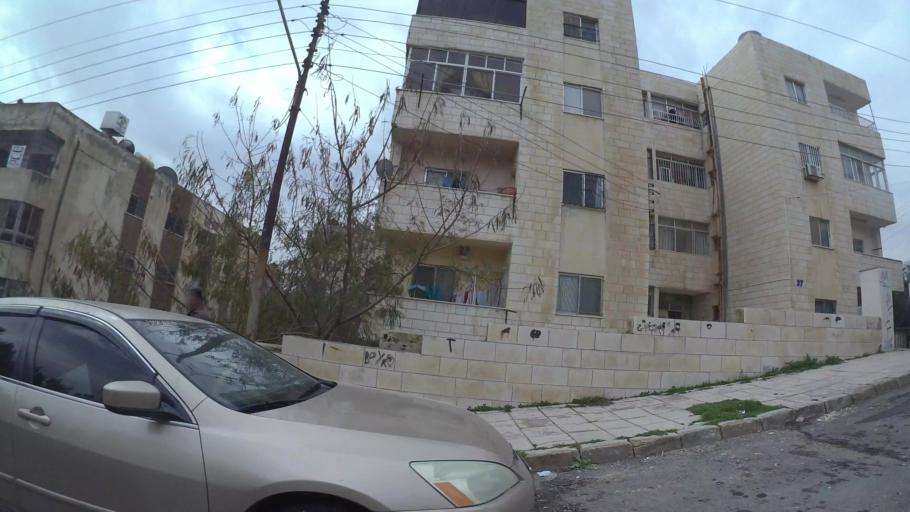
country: JO
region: Amman
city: Umm as Summaq
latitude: 31.9030
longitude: 35.8383
